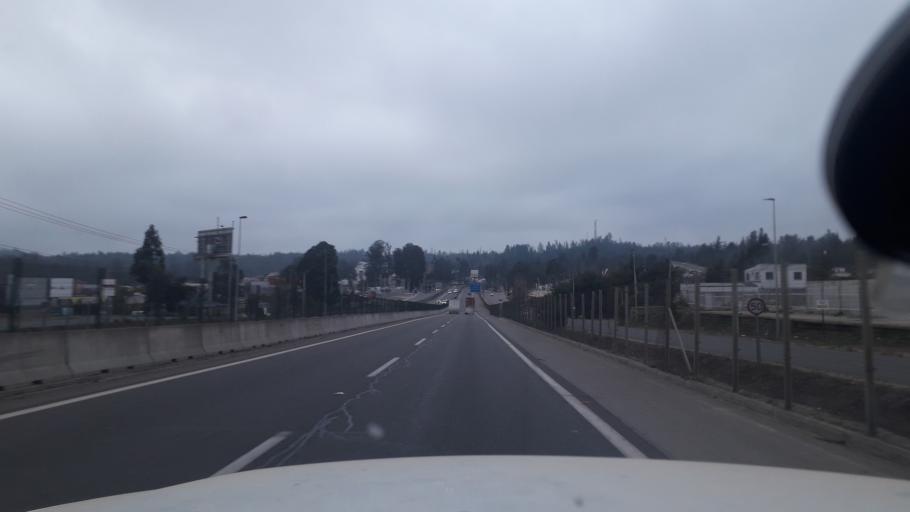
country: CL
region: Valparaiso
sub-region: Provincia de Valparaiso
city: Vina del Mar
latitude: -33.1183
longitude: -71.5606
